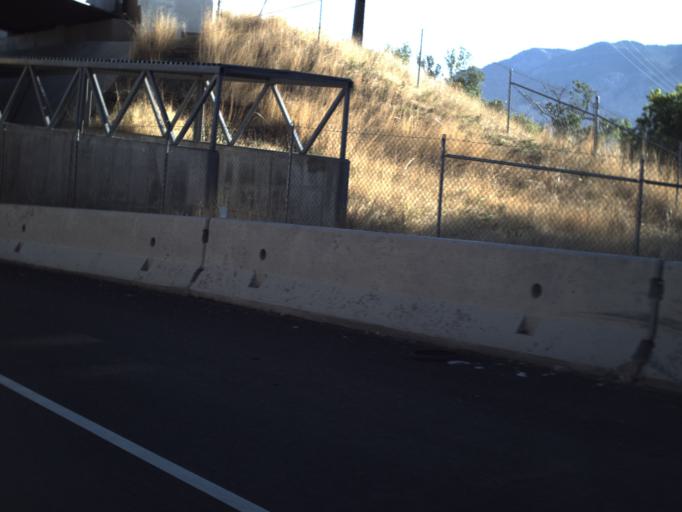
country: US
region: Utah
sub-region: Weber County
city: South Ogden
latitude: 41.2034
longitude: -111.9923
